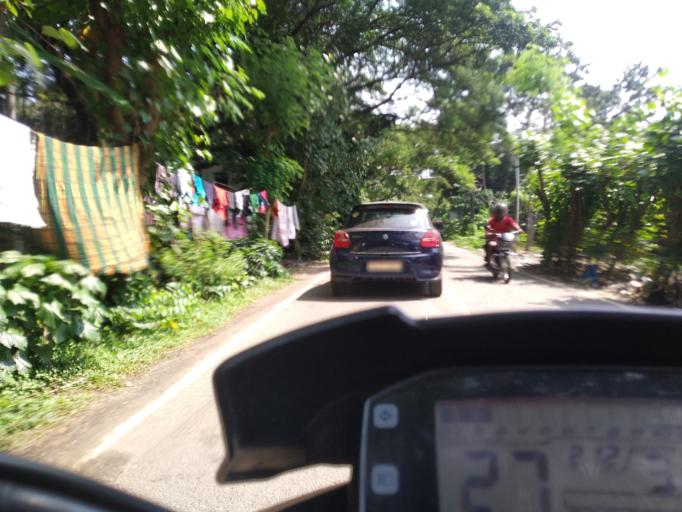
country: IN
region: Kerala
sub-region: Ernakulam
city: Cochin
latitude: 9.9730
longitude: 76.2932
